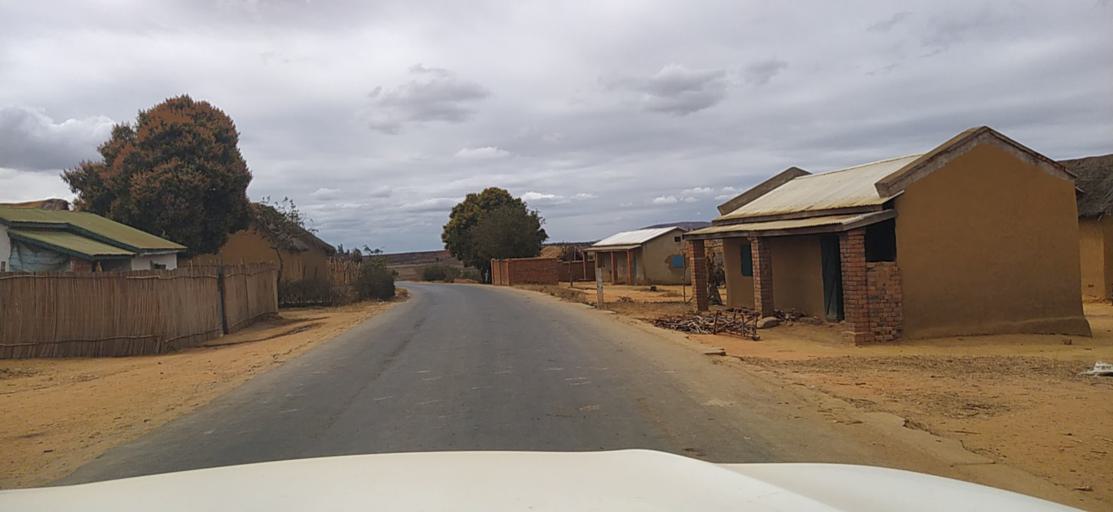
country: MG
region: Alaotra Mangoro
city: Ambatondrazaka
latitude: -17.9287
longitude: 48.2571
